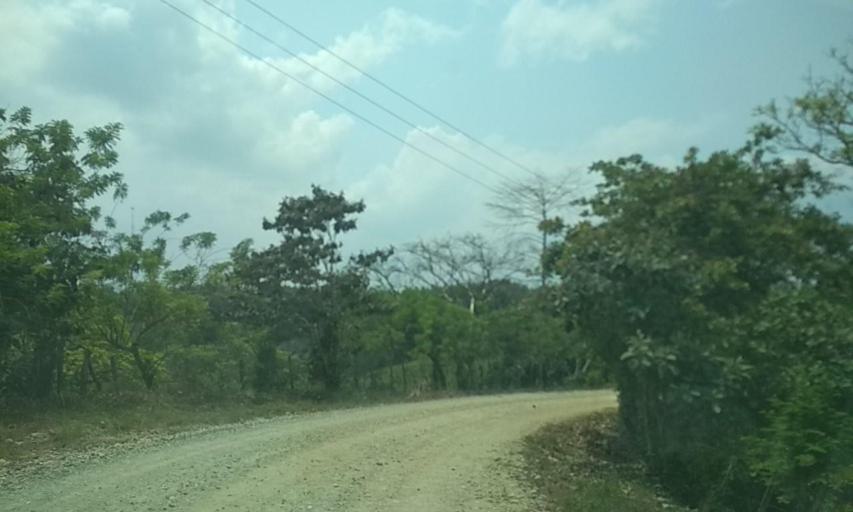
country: MX
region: Tabasco
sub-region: Huimanguillo
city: Francisco Rueda
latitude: 17.6379
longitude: -93.8228
